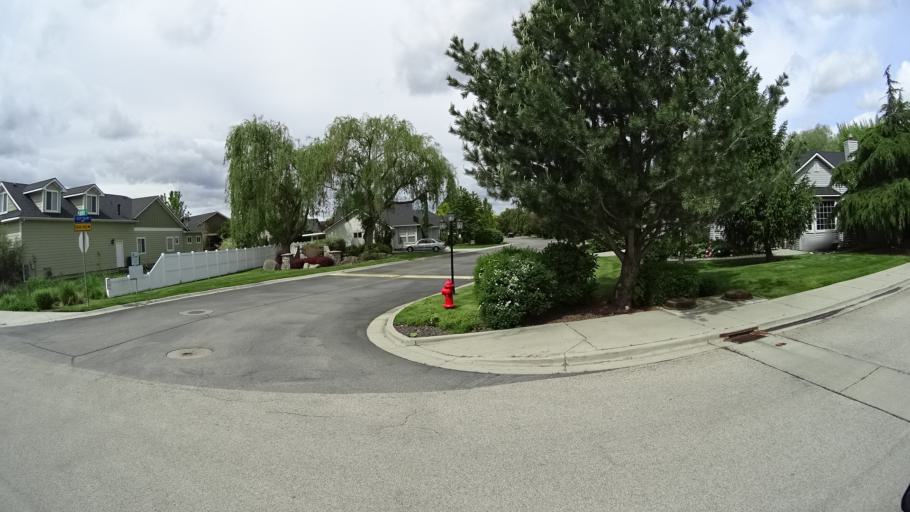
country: US
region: Idaho
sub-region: Ada County
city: Eagle
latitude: 43.6769
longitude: -116.3043
